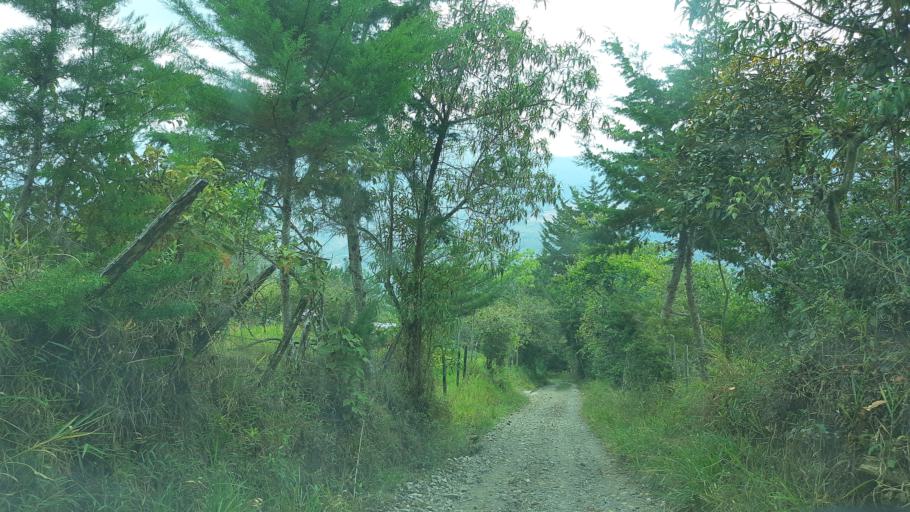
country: CO
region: Cundinamarca
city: Tenza
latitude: 5.0814
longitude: -73.3971
